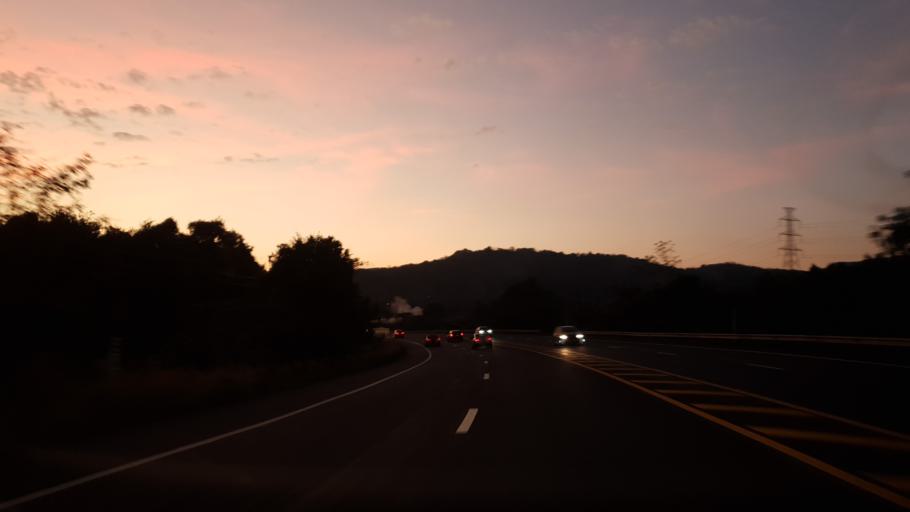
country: TH
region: Phitsanulok
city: Wang Thong
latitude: 16.8659
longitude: 100.4924
